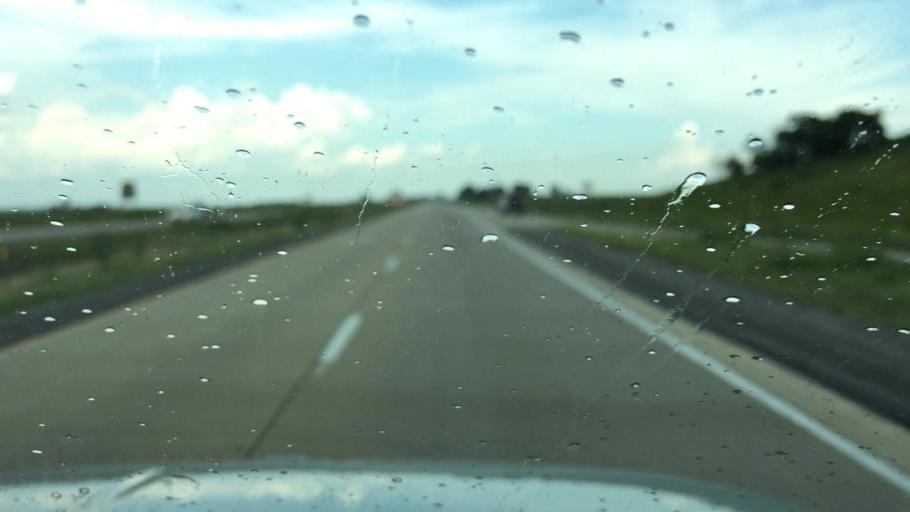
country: US
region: Iowa
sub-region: Poweshiek County
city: Brooklyn
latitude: 41.6961
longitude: -92.2745
